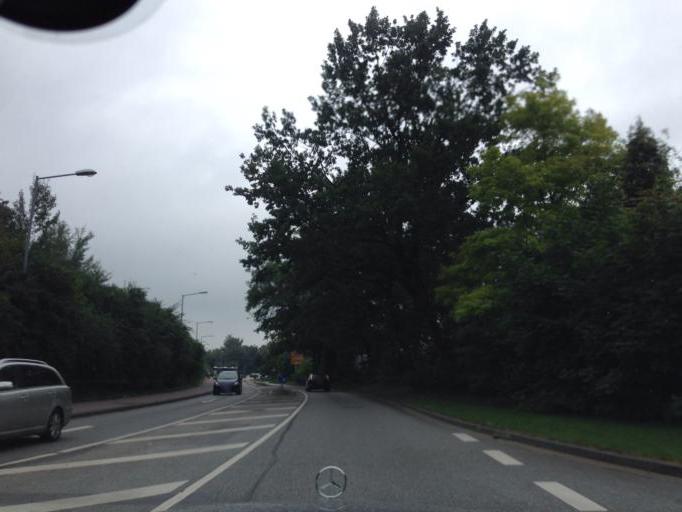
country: DE
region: Schleswig-Holstein
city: Barsbuettel
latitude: 53.5666
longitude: 10.1816
